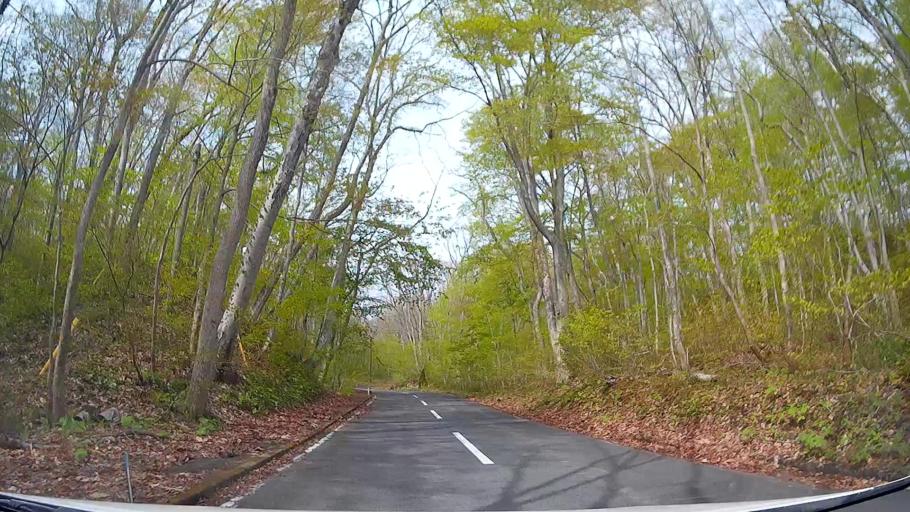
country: JP
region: Akita
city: Hanawa
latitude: 40.4318
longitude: 140.9151
